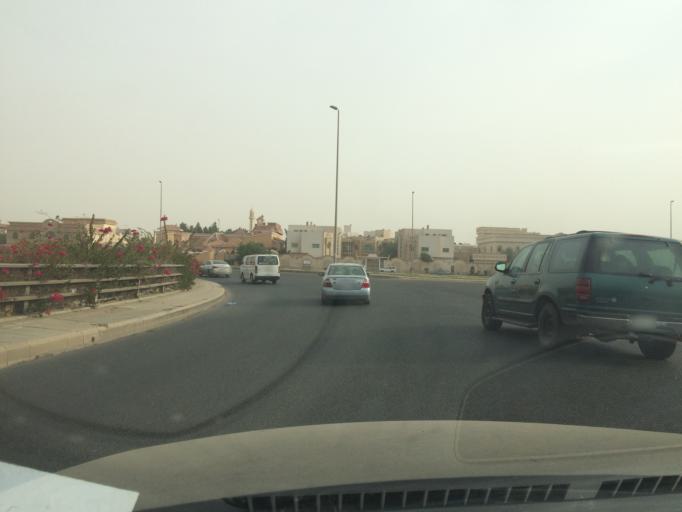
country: SA
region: Makkah
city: Jeddah
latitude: 21.4963
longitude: 39.2275
